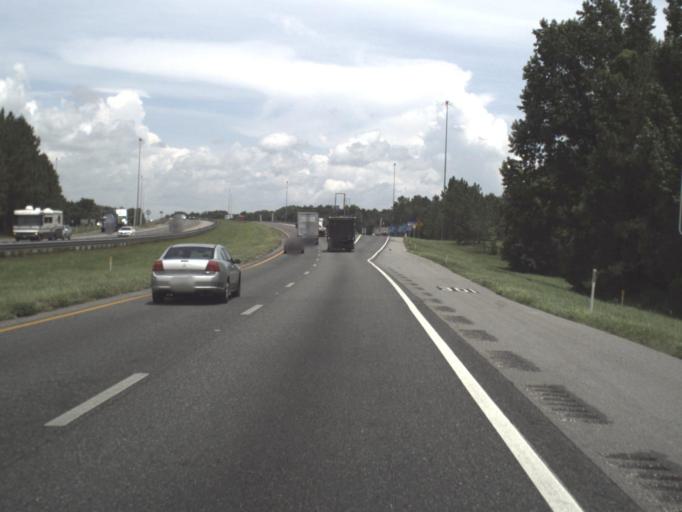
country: US
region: Florida
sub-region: Hernando County
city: Hill 'n Dale
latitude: 28.5187
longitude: -82.2374
